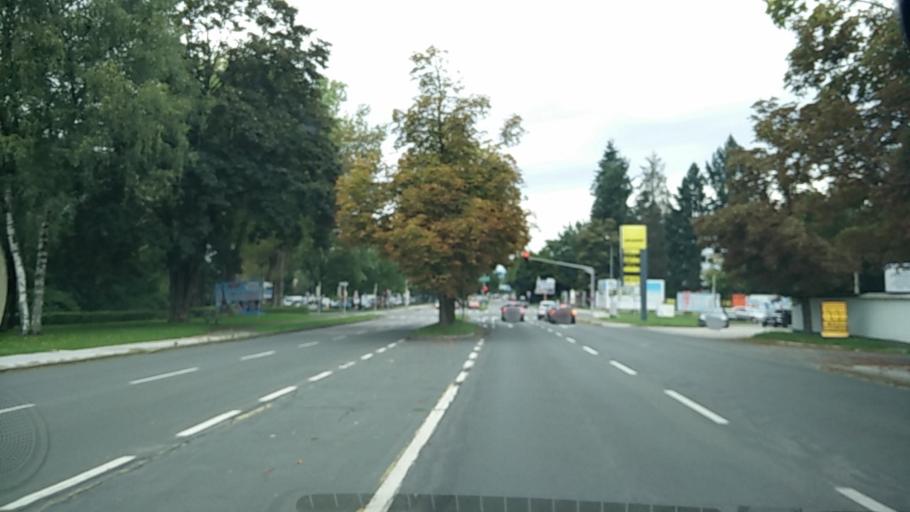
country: AT
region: Carinthia
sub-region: Klagenfurt am Woerthersee
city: Klagenfurt am Woerthersee
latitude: 46.6200
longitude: 14.2696
